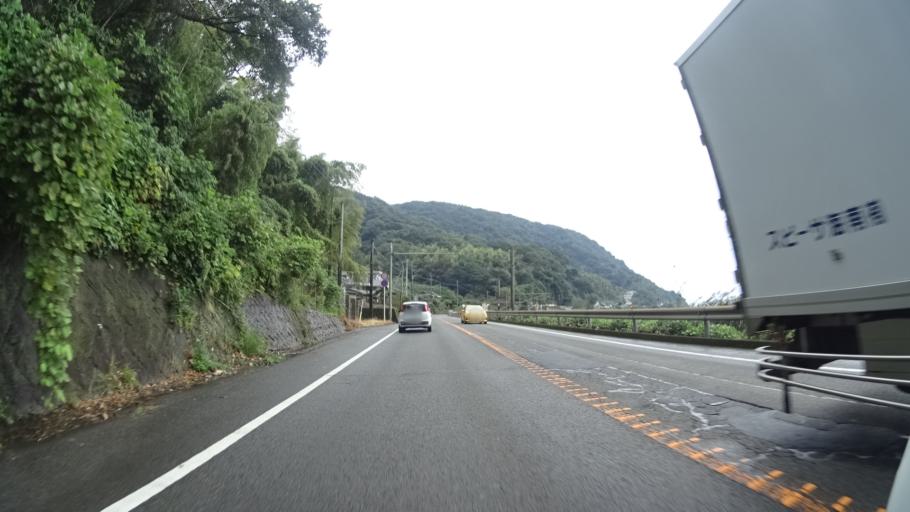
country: JP
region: Kagoshima
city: Kagoshima-shi
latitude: 31.6214
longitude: 130.5853
